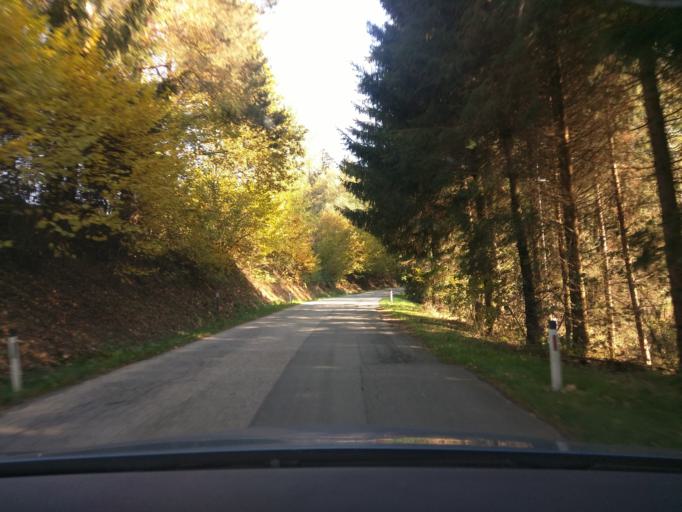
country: DE
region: Bavaria
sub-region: Lower Bavaria
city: Obernzell
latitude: 48.5357
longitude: 13.5570
